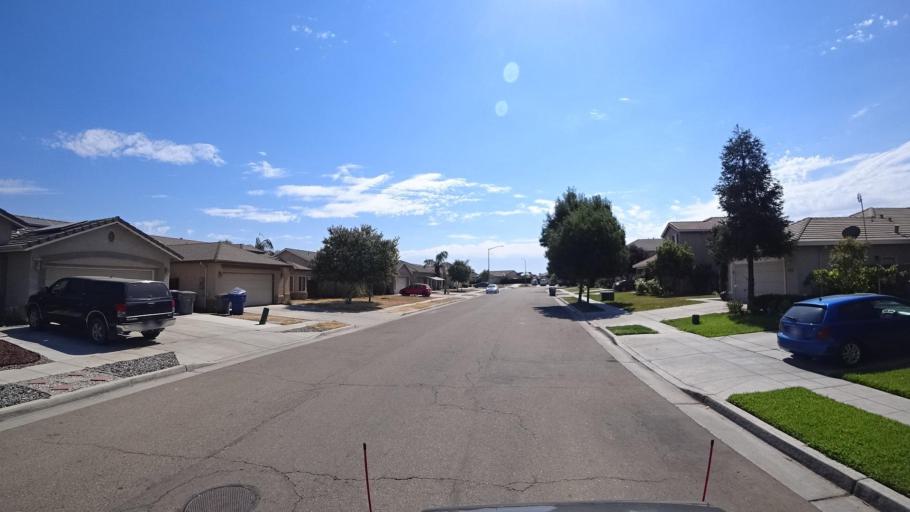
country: US
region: California
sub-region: Fresno County
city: Sunnyside
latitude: 36.7114
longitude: -119.7132
